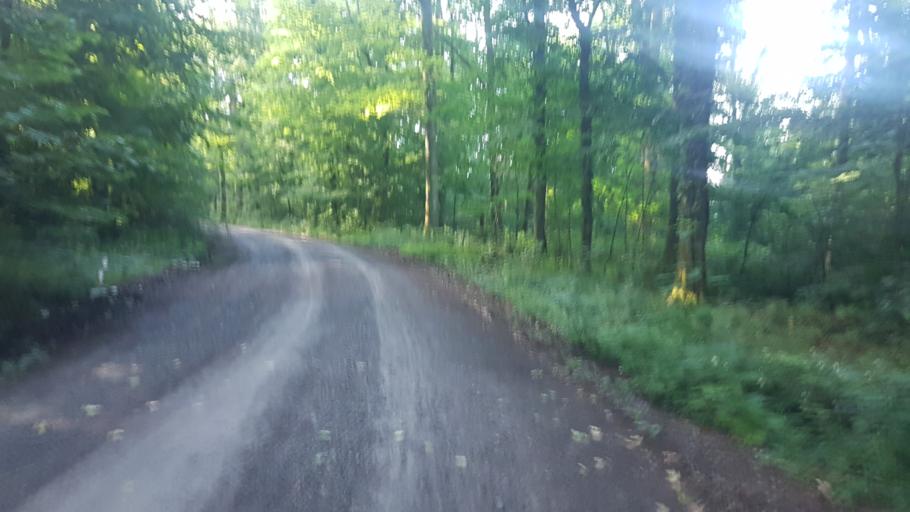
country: DE
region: Baden-Wuerttemberg
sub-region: Karlsruhe Region
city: Sternenfels
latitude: 49.0452
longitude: 8.8802
